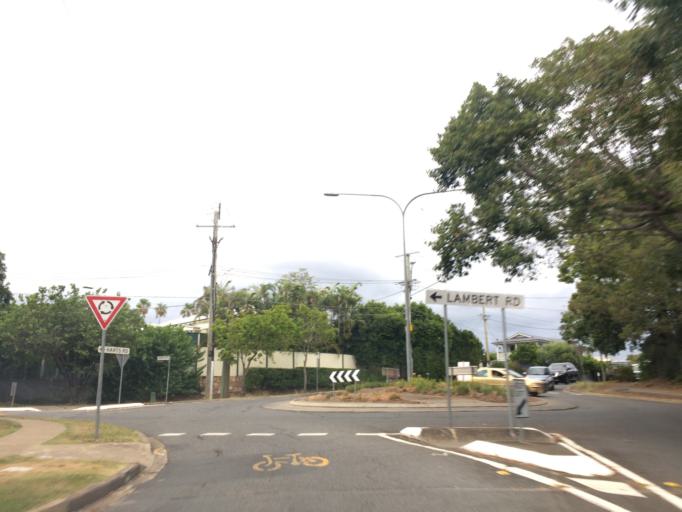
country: AU
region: Queensland
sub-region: Brisbane
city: Taringa
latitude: -27.5036
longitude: 152.9805
